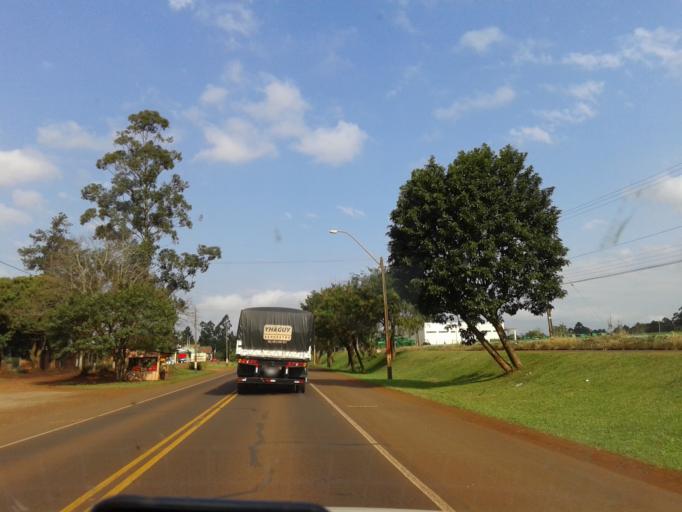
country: PY
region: Itapua
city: Arquitecto Tomas Romero Pereira
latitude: -26.4986
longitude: -55.2783
